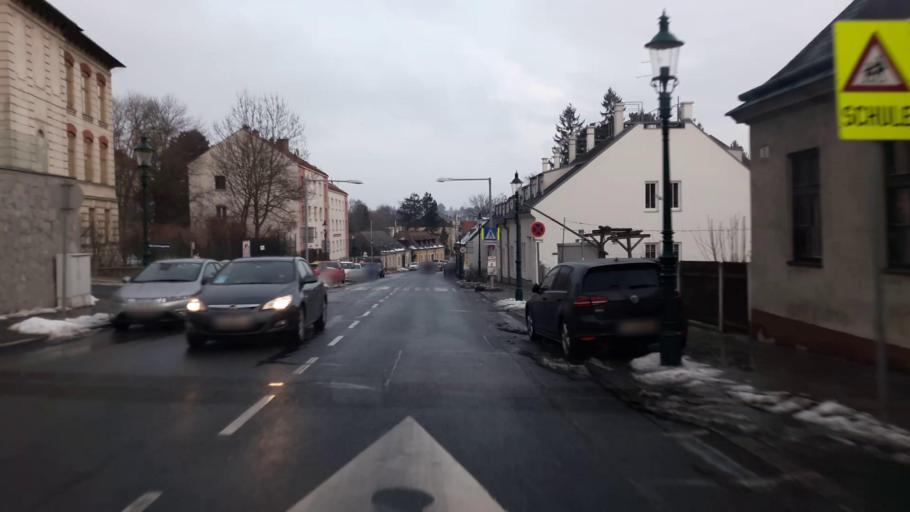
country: AT
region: Lower Austria
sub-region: Politischer Bezirk Wien-Umgebung
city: Klosterneuburg
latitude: 48.2519
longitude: 16.2958
